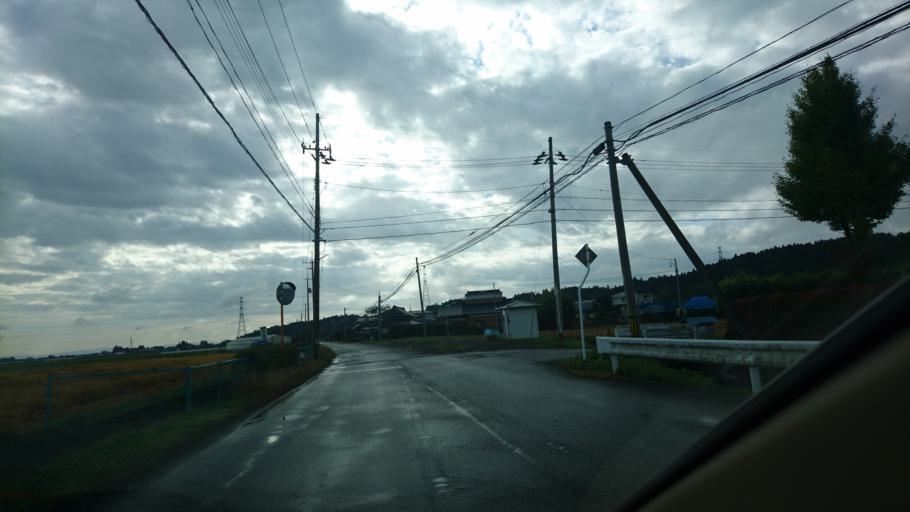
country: JP
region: Iwate
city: Ichinoseki
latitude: 38.7993
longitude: 140.9908
